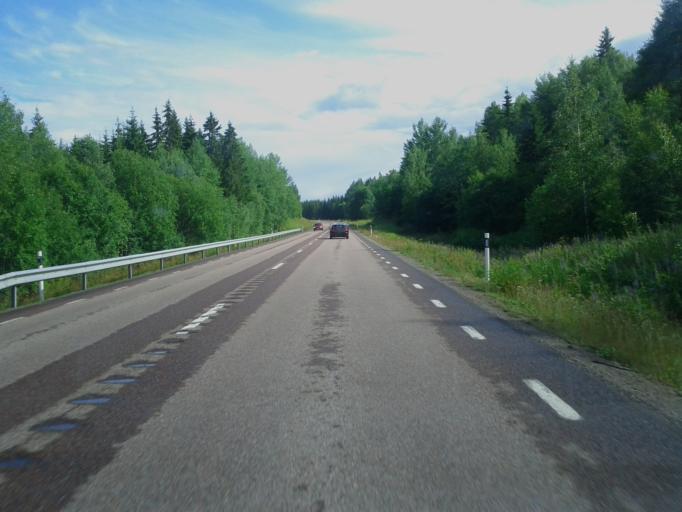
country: SE
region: Dalarna
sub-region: Faluns Kommun
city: Falun
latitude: 60.6568
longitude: 15.5539
